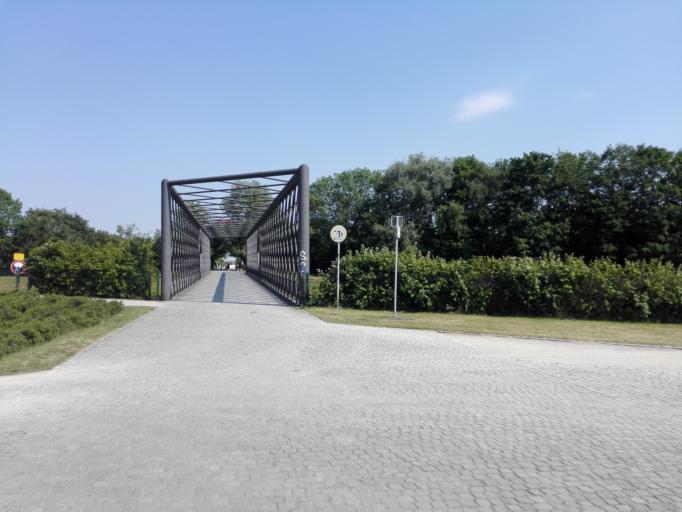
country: DE
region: North Rhine-Westphalia
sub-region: Regierungsbezirk Munster
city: Gladbeck
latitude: 51.5236
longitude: 7.0313
